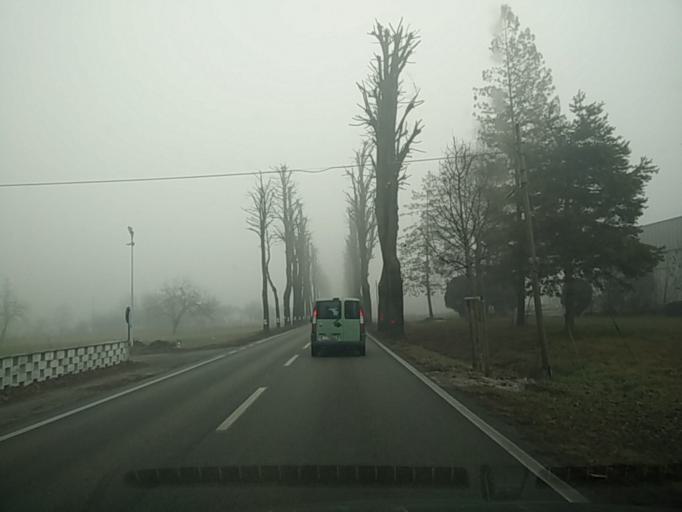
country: IT
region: Veneto
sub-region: Provincia di Belluno
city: Seren del Grappa
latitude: 46.0066
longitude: 11.8522
